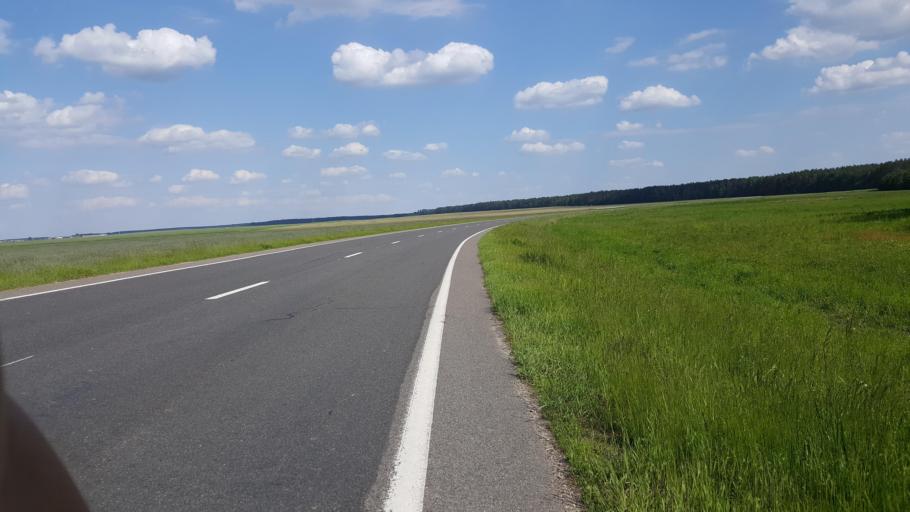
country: BY
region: Brest
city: Pruzhany
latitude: 52.5482
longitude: 24.1521
